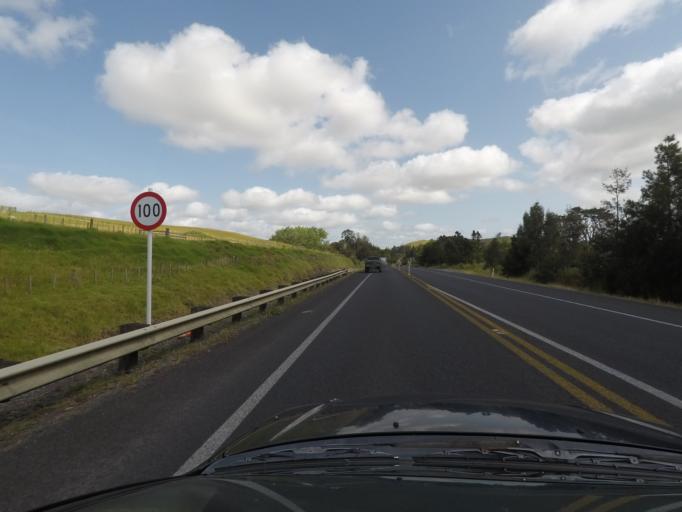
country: NZ
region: Northland
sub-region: Whangarei
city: Whangarei
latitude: -35.8316
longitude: 174.3145
